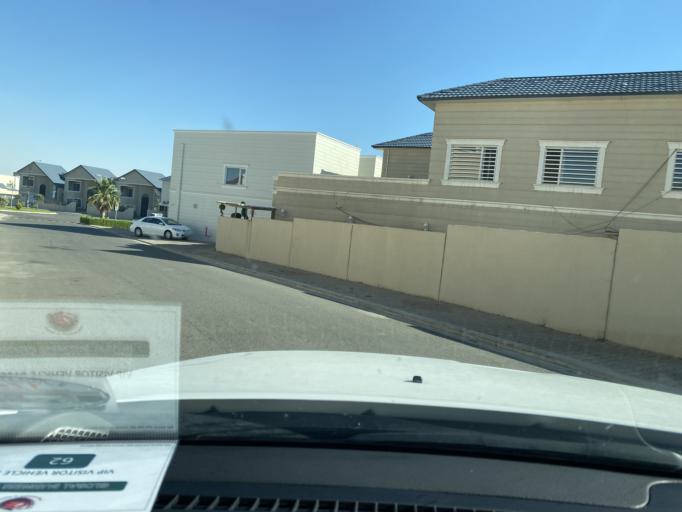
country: IQ
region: Arbil
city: Erbil
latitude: 36.2443
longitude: 44.0474
